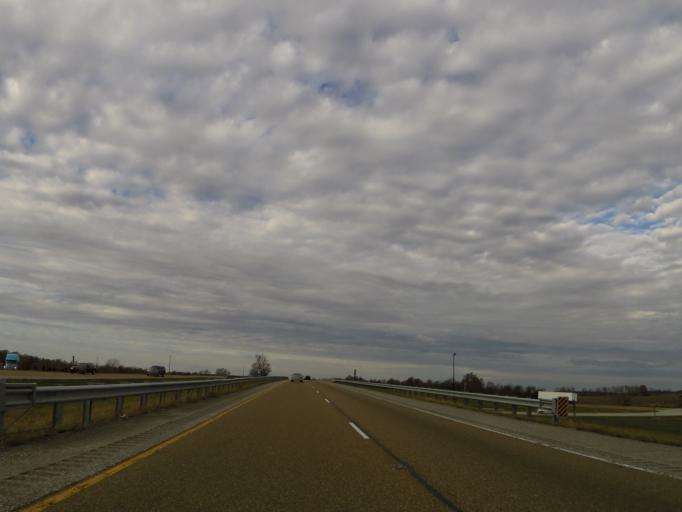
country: US
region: Illinois
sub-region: Clinton County
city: Wamac
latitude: 38.3893
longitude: -89.1683
